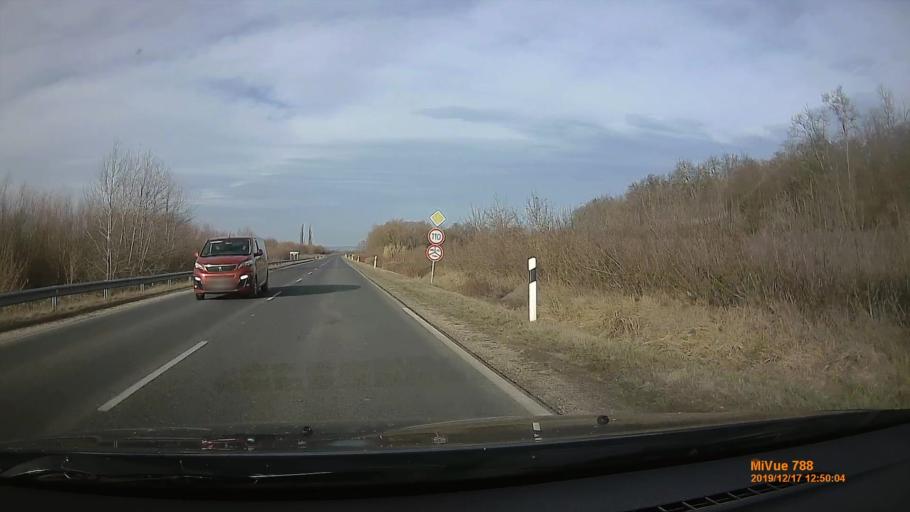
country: HU
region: Somogy
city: Balatonlelle
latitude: 46.7658
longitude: 17.7604
